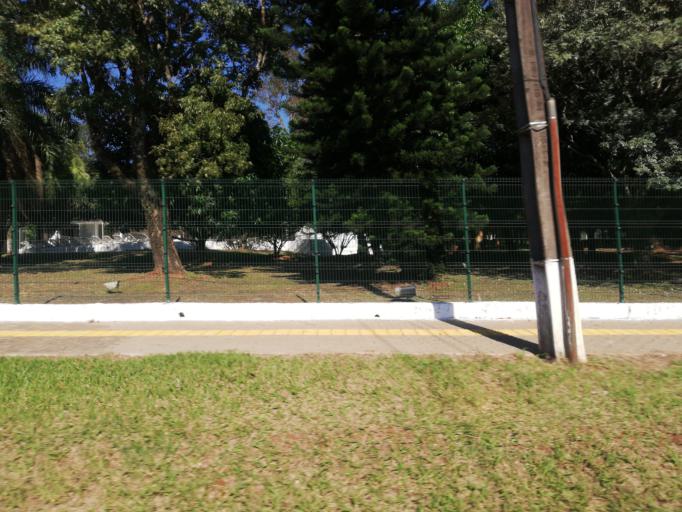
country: BR
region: Parana
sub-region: Foz Do Iguacu
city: Foz do Iguacu
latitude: -25.5562
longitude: -54.5649
